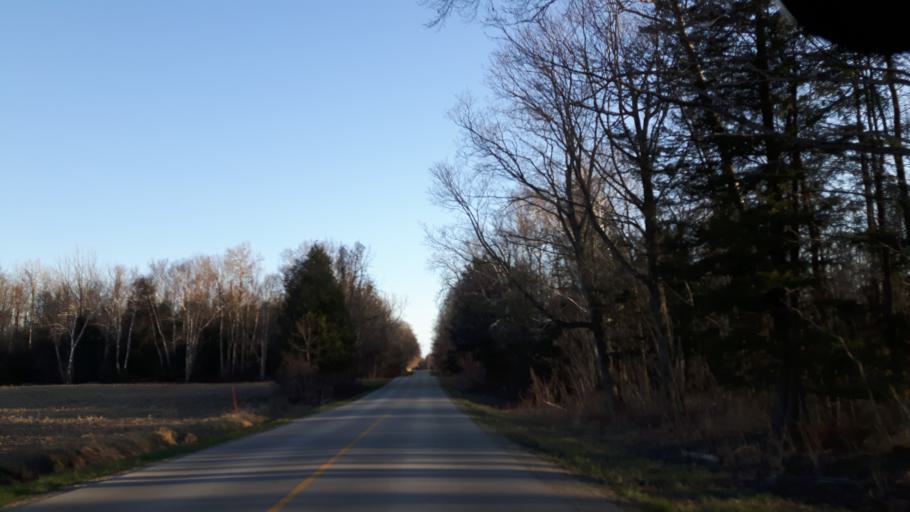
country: CA
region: Ontario
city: Goderich
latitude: 43.6203
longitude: -81.6847
